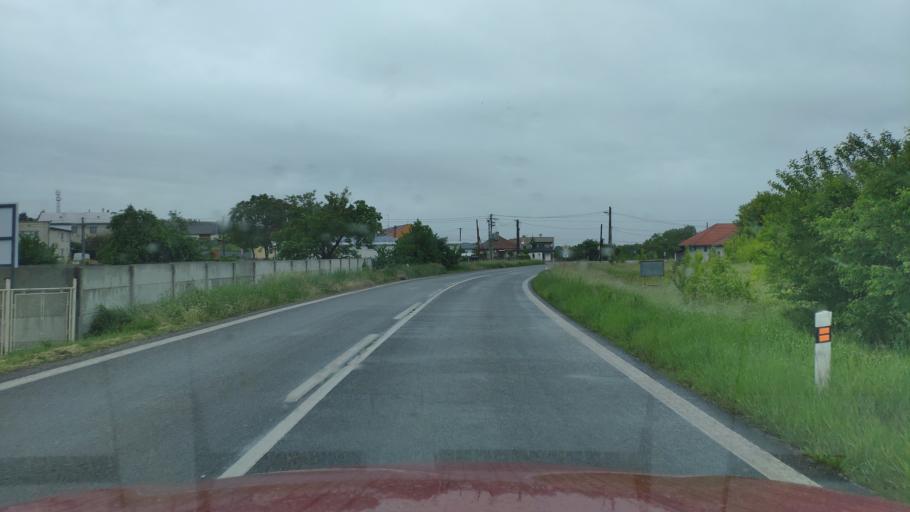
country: HU
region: Borsod-Abauj-Zemplen
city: Karcsa
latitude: 48.4025
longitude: 21.8107
